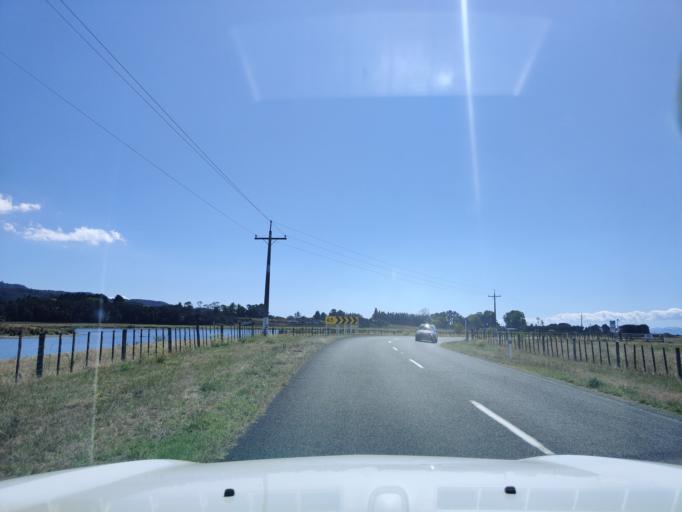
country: NZ
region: Waikato
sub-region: Thames-Coromandel District
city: Thames
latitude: -37.0605
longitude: 175.2982
